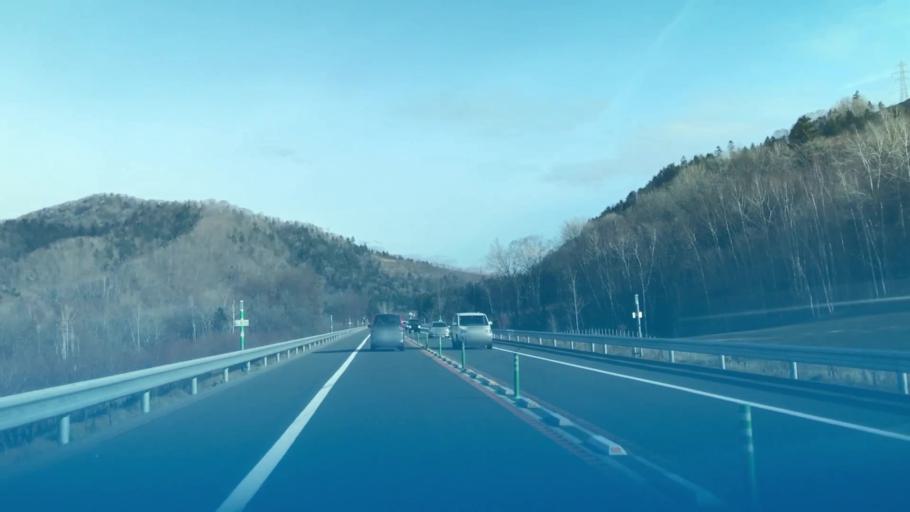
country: JP
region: Hokkaido
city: Shimo-furano
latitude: 43.0160
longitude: 142.4329
